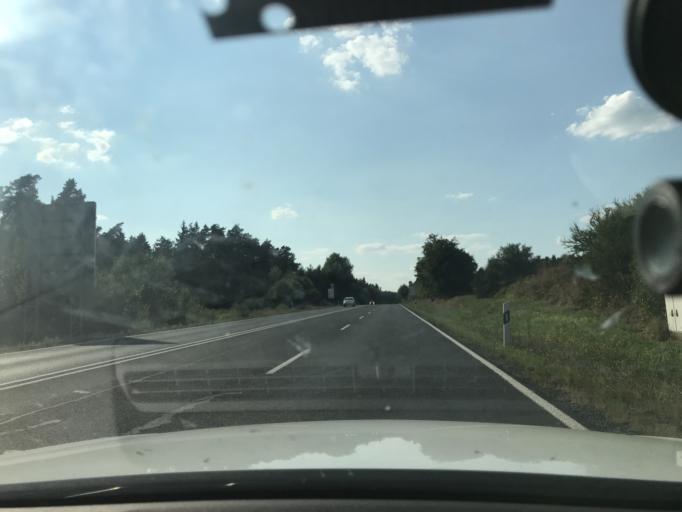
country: DE
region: Bavaria
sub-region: Upper Palatinate
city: Poppenricht
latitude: 49.4658
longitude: 11.7791
